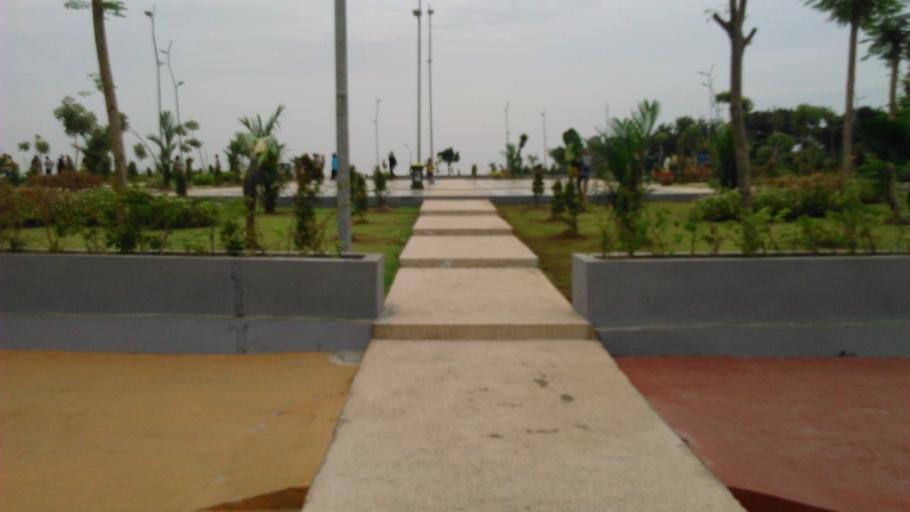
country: ID
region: East Java
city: Labansari
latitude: -7.2251
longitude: 112.7875
